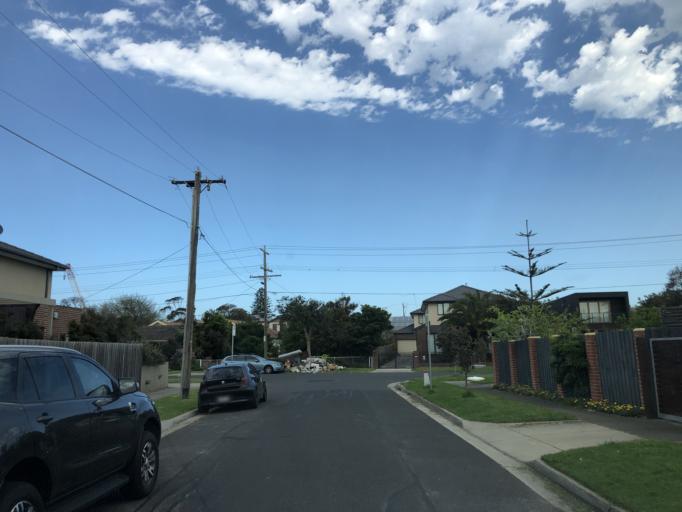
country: AU
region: Victoria
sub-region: Kingston
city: Carrum
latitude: -38.0764
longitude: 145.1255
